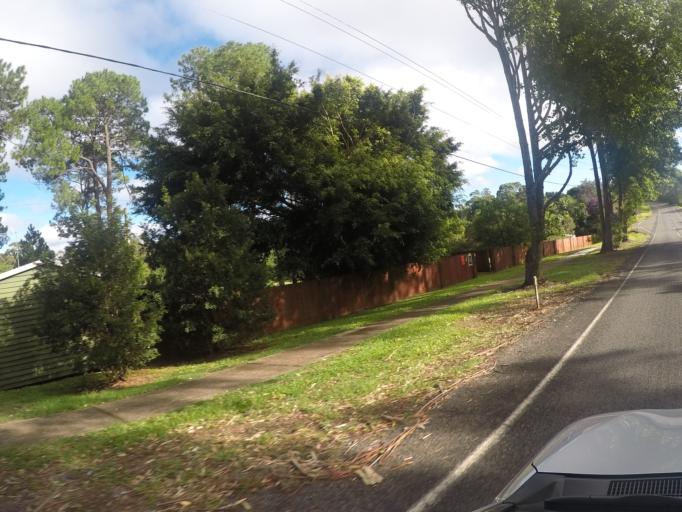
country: AU
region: Queensland
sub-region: Sunshine Coast
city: Nambour
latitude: -26.6312
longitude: 152.8675
